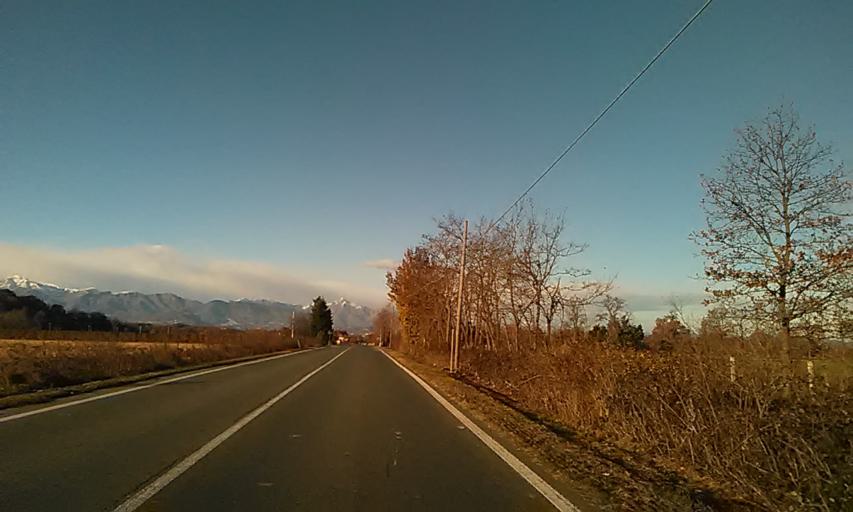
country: IT
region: Piedmont
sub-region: Provincia di Biella
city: Gifflenga
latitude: 45.4790
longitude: 8.2183
